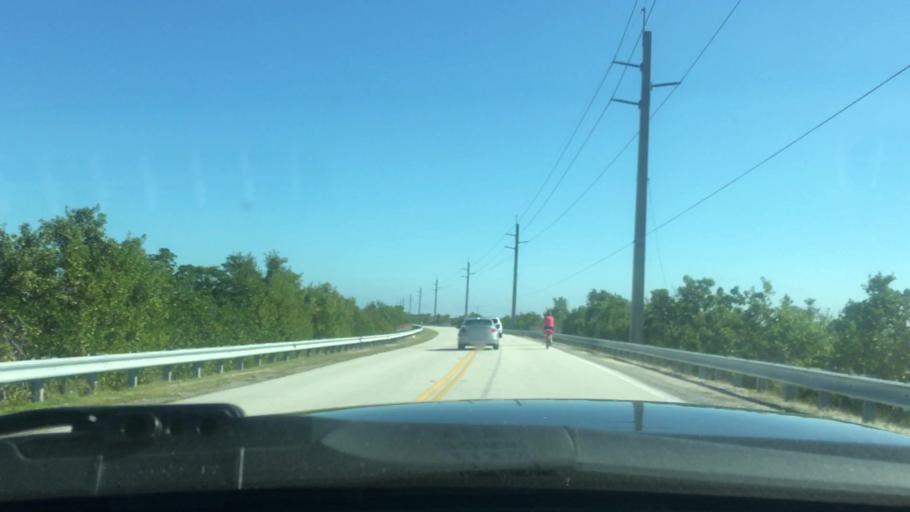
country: US
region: Florida
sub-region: Monroe County
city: North Key Largo
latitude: 25.2842
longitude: -80.3123
